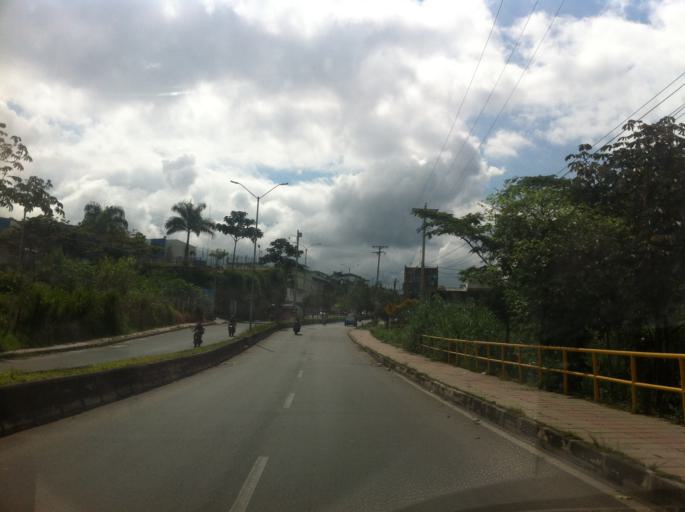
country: CO
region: Quindio
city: Armenia
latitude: 4.5170
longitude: -75.7031
